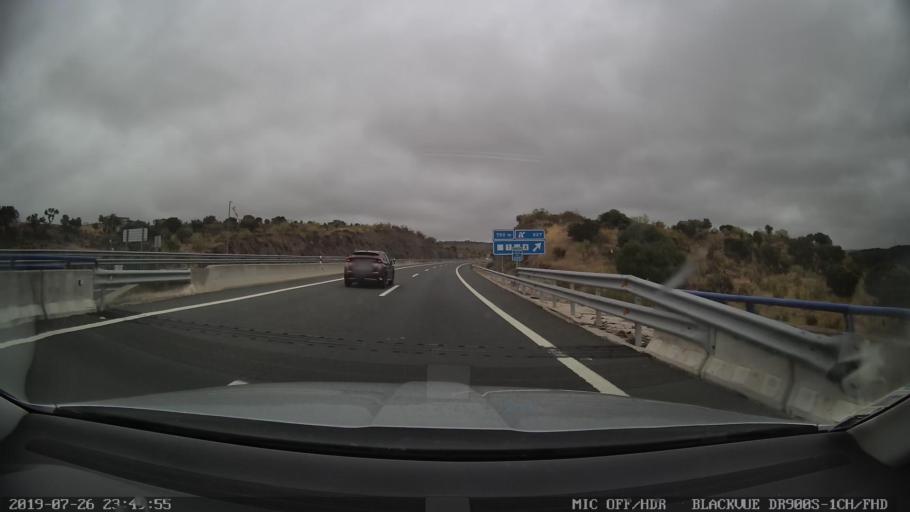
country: ES
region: Extremadura
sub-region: Provincia de Caceres
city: Jaraicejo
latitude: 39.6513
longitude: -5.8062
